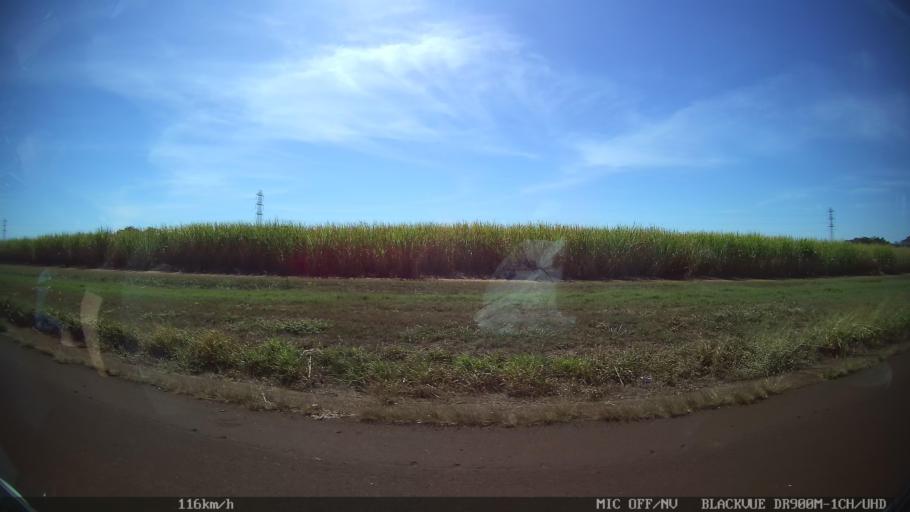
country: BR
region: Sao Paulo
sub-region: Guaira
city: Guaira
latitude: -20.4452
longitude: -48.2271
